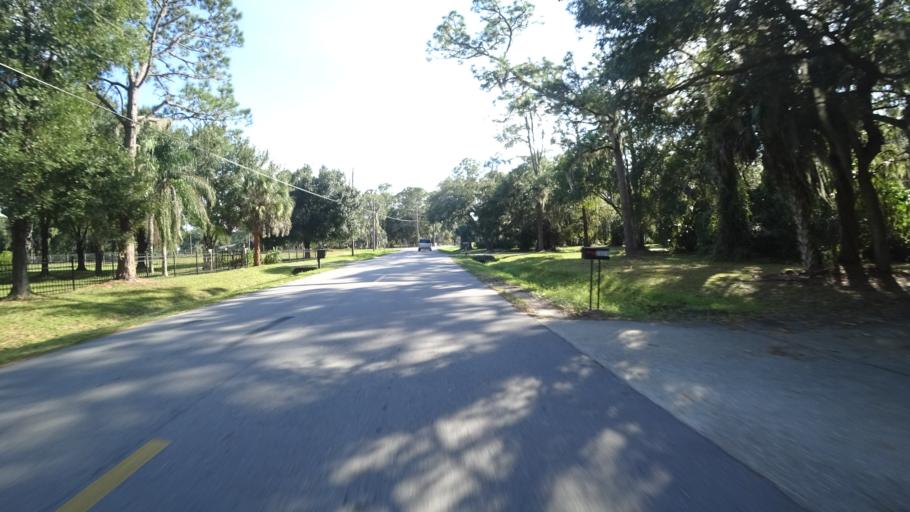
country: US
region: Florida
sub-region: Manatee County
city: Samoset
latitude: 27.4647
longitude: -82.4741
